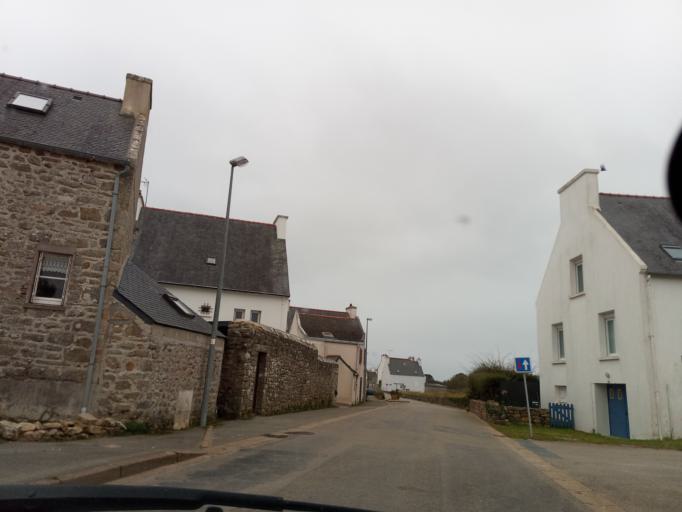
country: FR
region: Brittany
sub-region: Departement du Finistere
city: Esquibien
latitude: 48.0232
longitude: -4.5631
